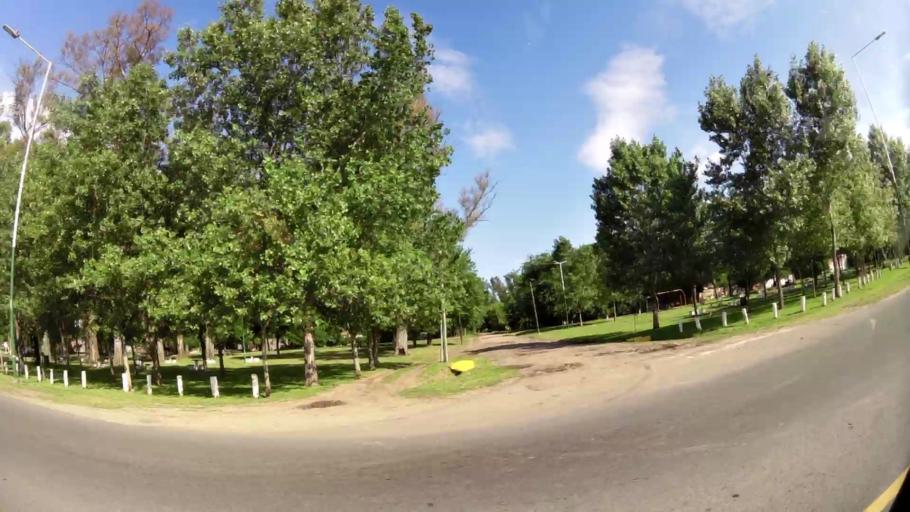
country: AR
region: Buenos Aires
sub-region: Partido de Merlo
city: Merlo
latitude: -34.6535
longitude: -58.7483
